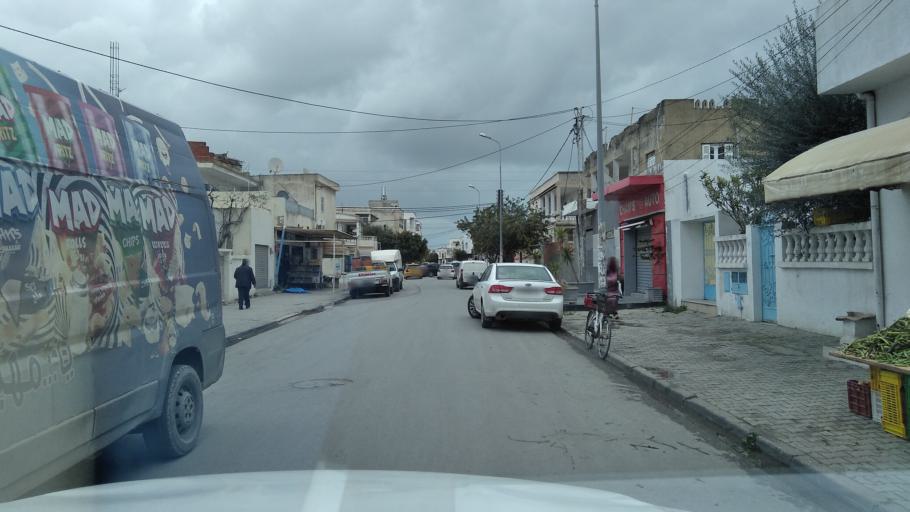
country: TN
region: Bin 'Arus
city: Ben Arous
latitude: 36.7580
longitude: 10.2241
